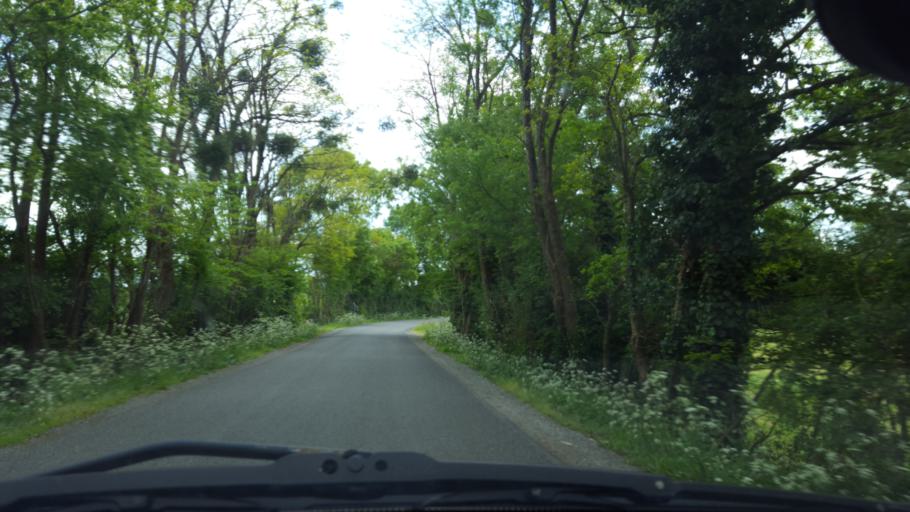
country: FR
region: Pays de la Loire
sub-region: Departement de la Loire-Atlantique
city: Saint-Philbert-de-Grand-Lieu
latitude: 47.0366
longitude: -1.6022
